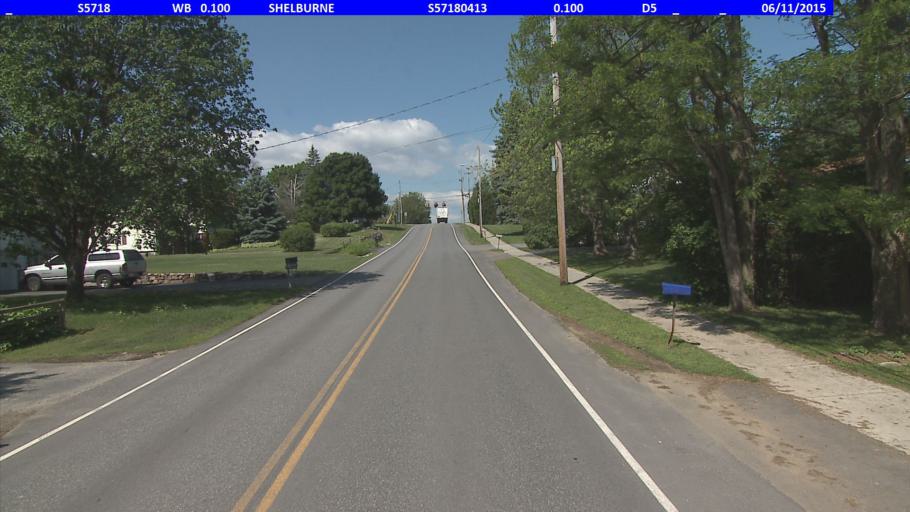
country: US
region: Vermont
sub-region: Chittenden County
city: Burlington
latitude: 44.3697
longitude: -73.2297
